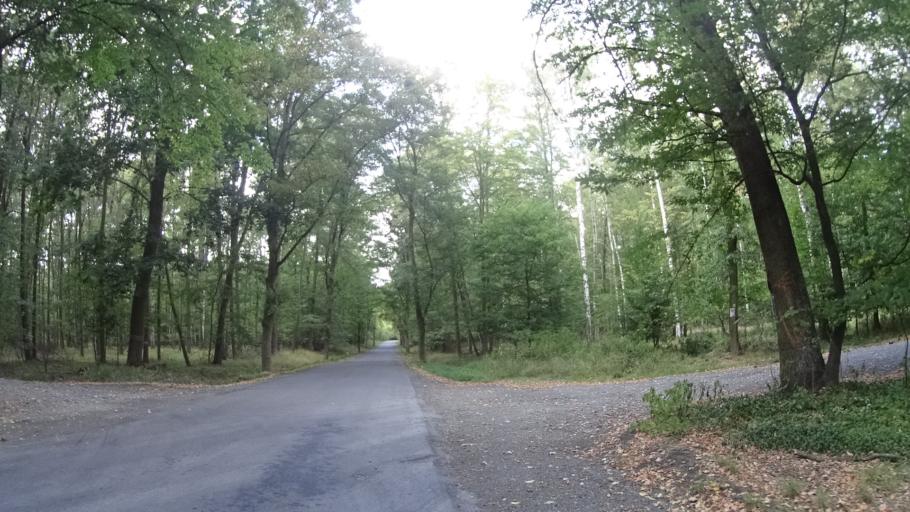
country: CZ
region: Olomoucky
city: Bila Lhota
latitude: 49.7285
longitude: 17.0128
